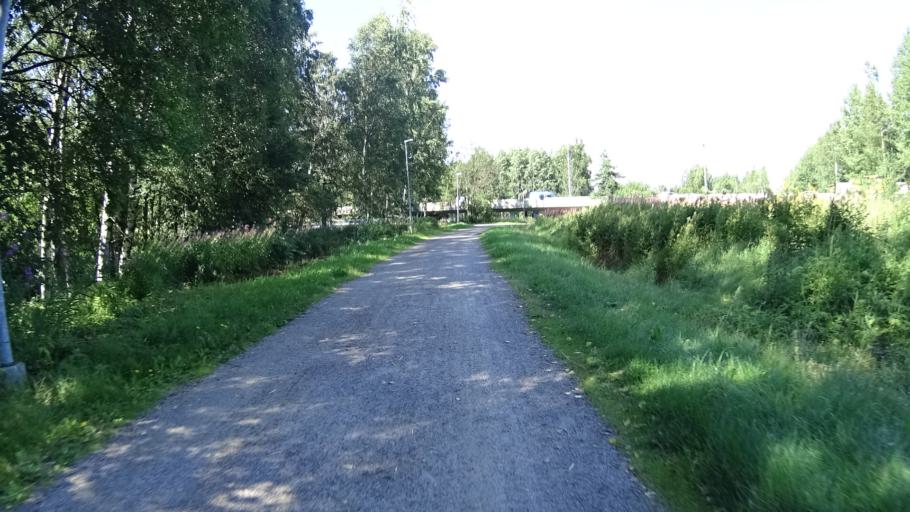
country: FI
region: Uusimaa
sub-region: Helsinki
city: Teekkarikylae
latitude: 60.2337
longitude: 24.8679
